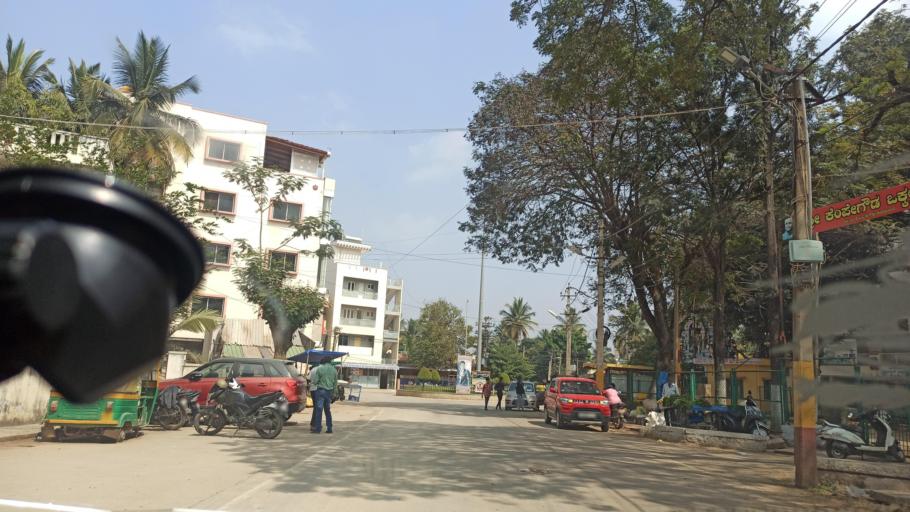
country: IN
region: Karnataka
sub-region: Bangalore Urban
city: Yelahanka
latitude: 13.0789
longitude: 77.6070
